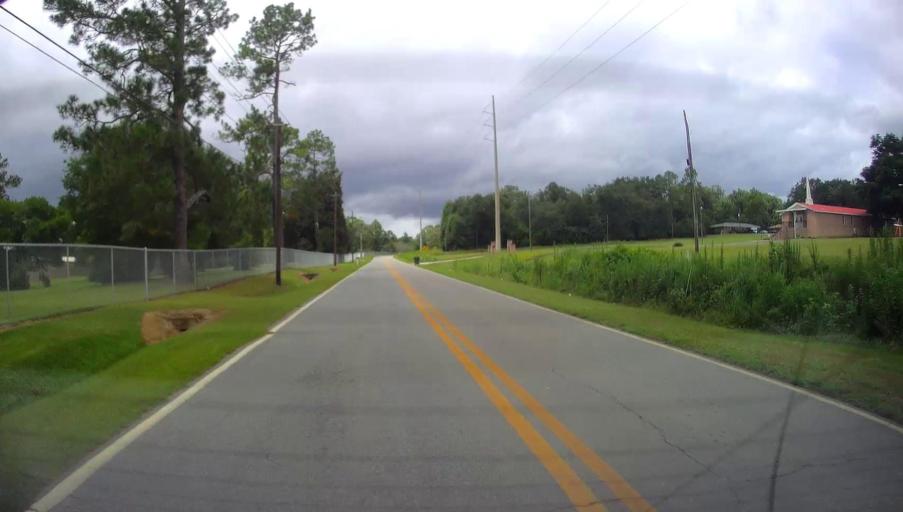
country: US
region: Georgia
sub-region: Bibb County
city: Macon
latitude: 32.8043
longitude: -83.5362
